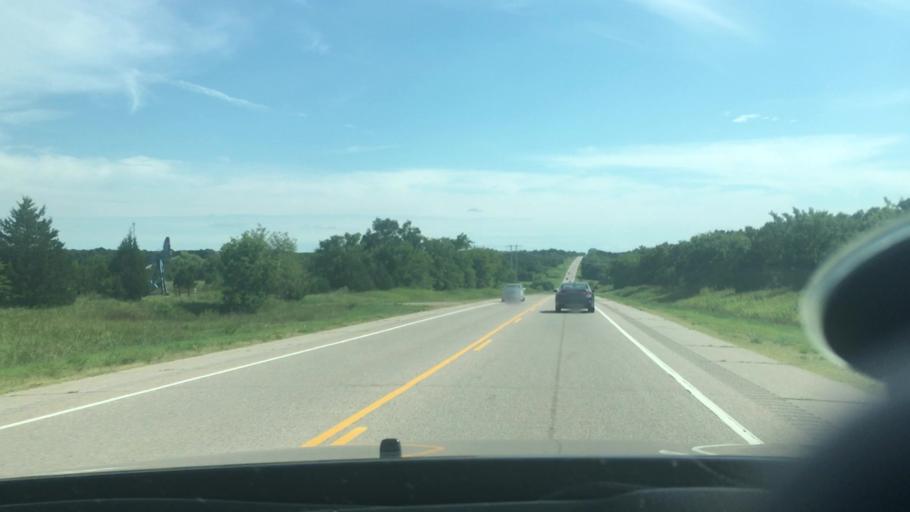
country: US
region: Oklahoma
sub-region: Seminole County
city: Konawa
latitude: 35.0343
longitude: -96.6783
